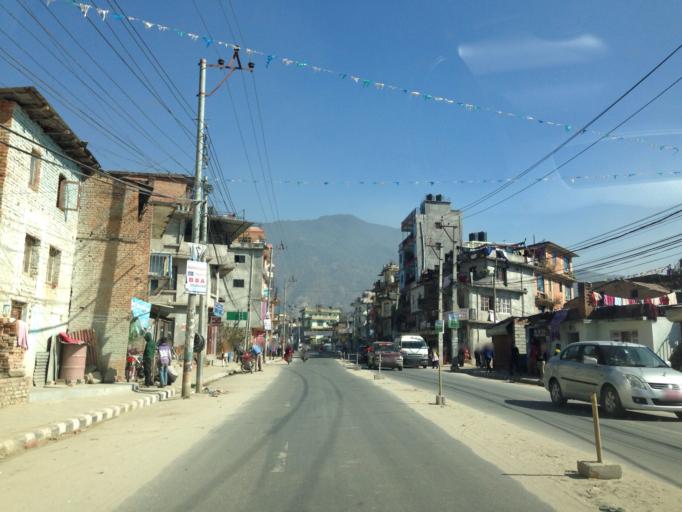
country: NP
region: Central Region
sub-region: Bagmati Zone
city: Kathmandu
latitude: 27.7669
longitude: 85.3544
